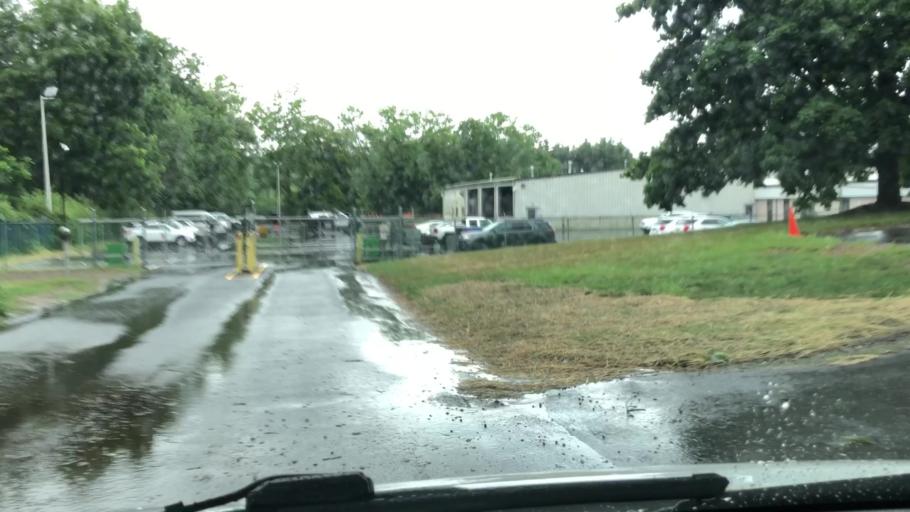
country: US
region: Massachusetts
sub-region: Berkshire County
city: Dalton
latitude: 42.4719
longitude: -73.2046
